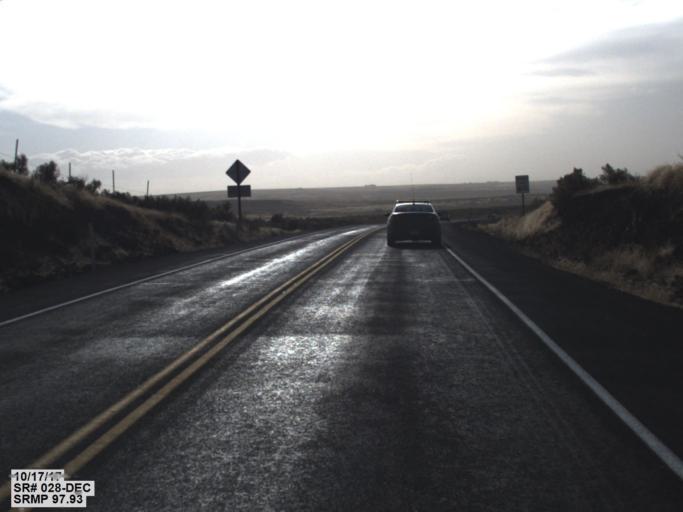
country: US
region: Washington
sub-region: Adams County
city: Ritzville
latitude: 47.3427
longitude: -118.6089
